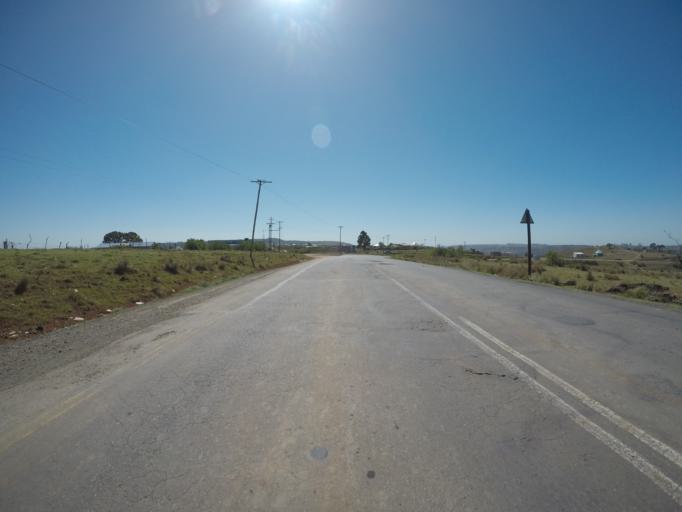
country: ZA
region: Eastern Cape
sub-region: OR Tambo District Municipality
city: Mthatha
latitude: -31.8943
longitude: 28.9422
